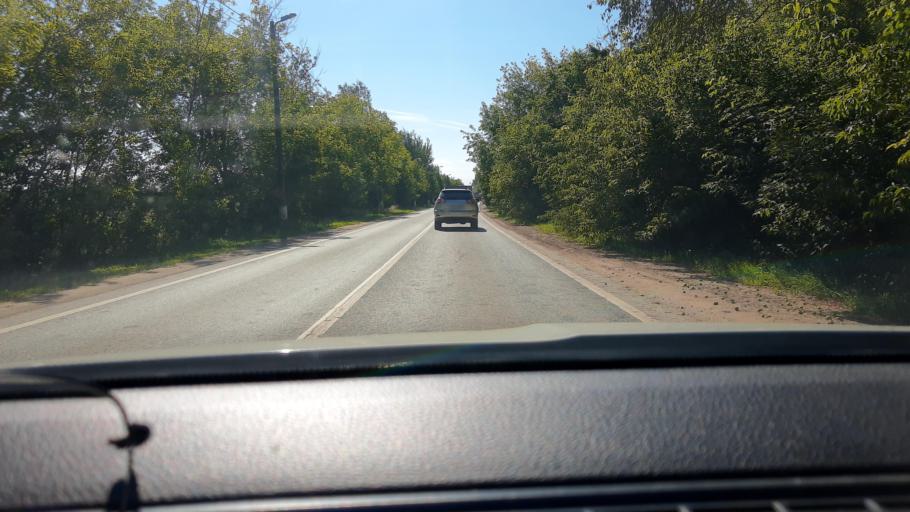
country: RU
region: Moskovskaya
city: Petrovo-Dal'neye
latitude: 55.7638
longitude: 37.2265
